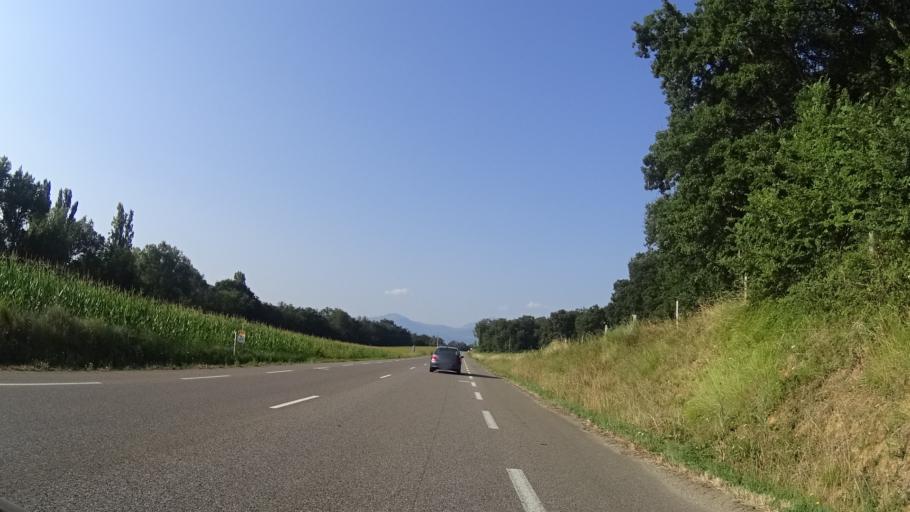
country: FR
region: Midi-Pyrenees
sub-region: Departement de l'Ariege
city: Mirepoix
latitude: 43.0204
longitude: 1.8925
